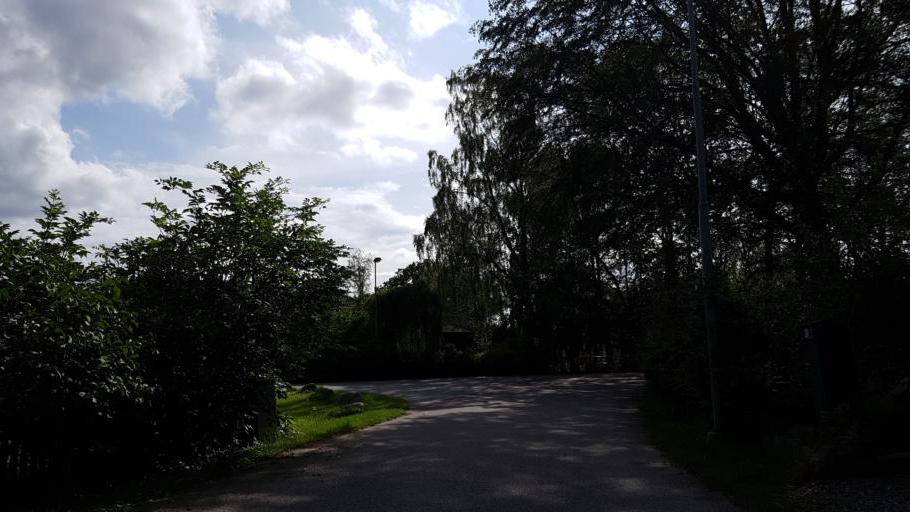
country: SE
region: Vaestra Goetaland
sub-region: Harryda Kommun
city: Molnlycke
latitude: 57.6633
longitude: 12.1073
